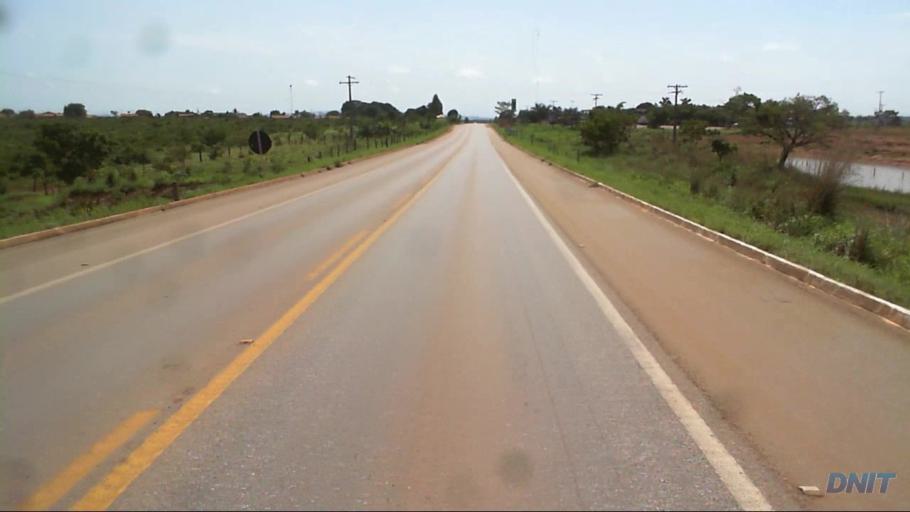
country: BR
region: Goias
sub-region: Barro Alto
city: Barro Alto
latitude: -15.2079
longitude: -48.7061
